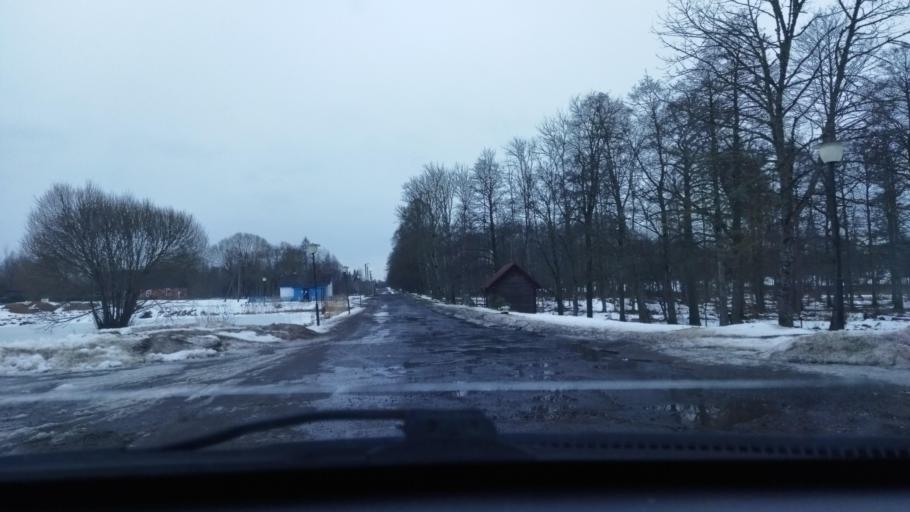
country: BY
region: Minsk
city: Svir
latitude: 54.9014
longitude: 26.4004
